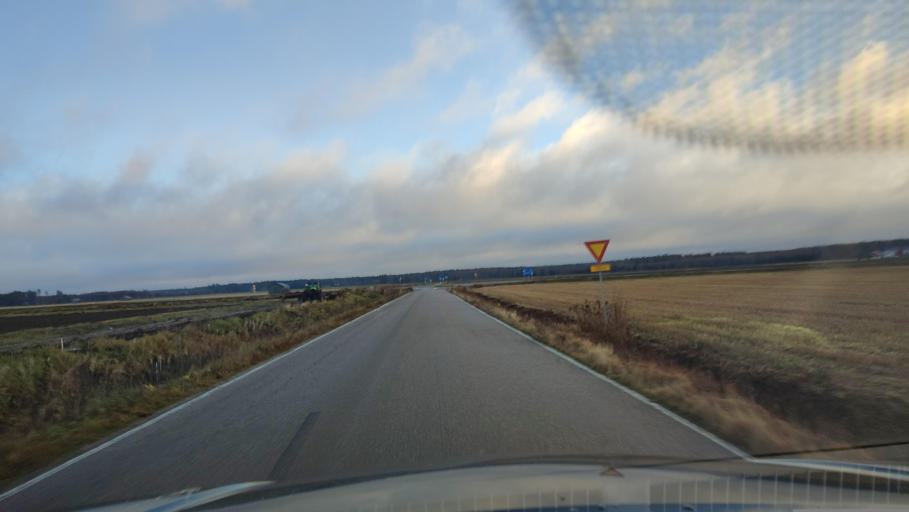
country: FI
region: Ostrobothnia
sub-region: Sydosterbotten
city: Naerpes
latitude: 62.4463
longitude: 21.4242
